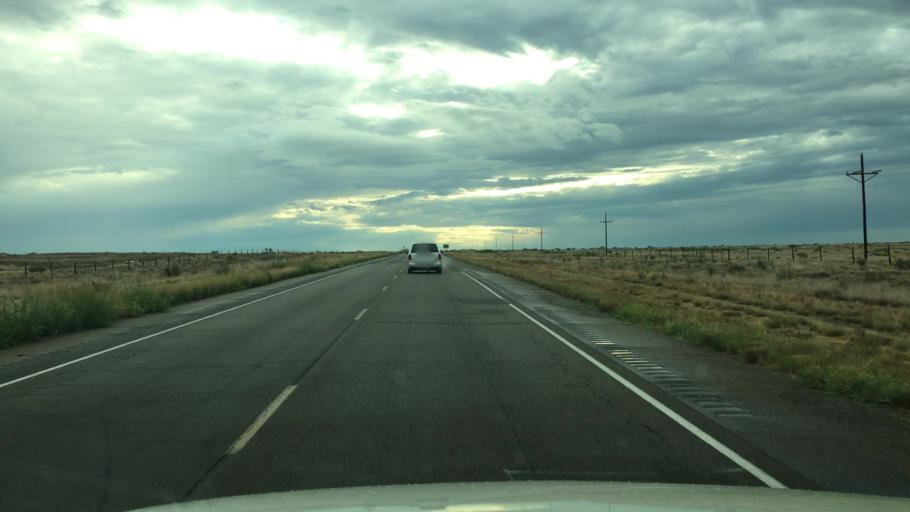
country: US
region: New Mexico
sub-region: Chaves County
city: Roswell
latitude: 33.4027
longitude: -104.3258
